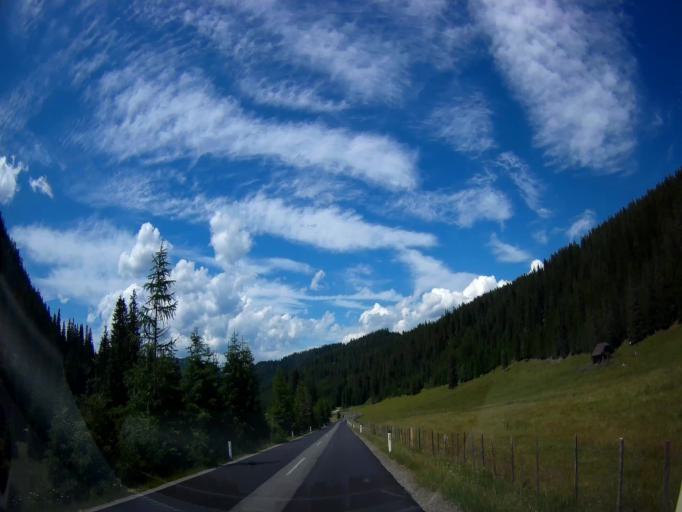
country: AT
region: Carinthia
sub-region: Politischer Bezirk Sankt Veit an der Glan
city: Glodnitz
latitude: 46.9565
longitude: 14.0249
